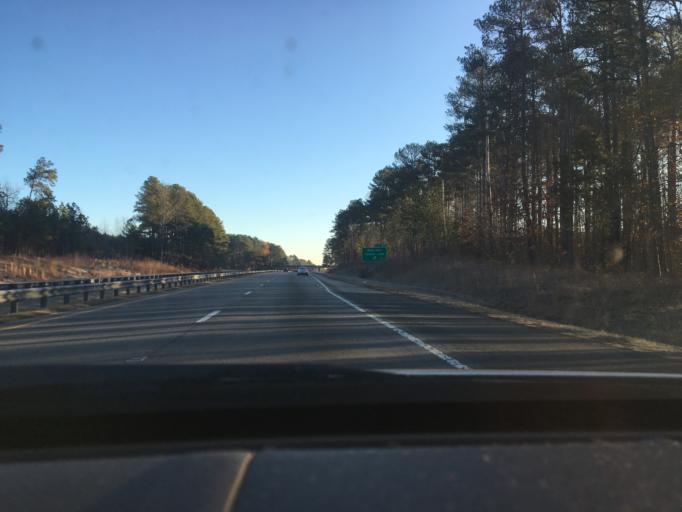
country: US
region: North Carolina
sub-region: Wake County
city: Holly Springs
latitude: 35.6664
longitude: -78.9355
